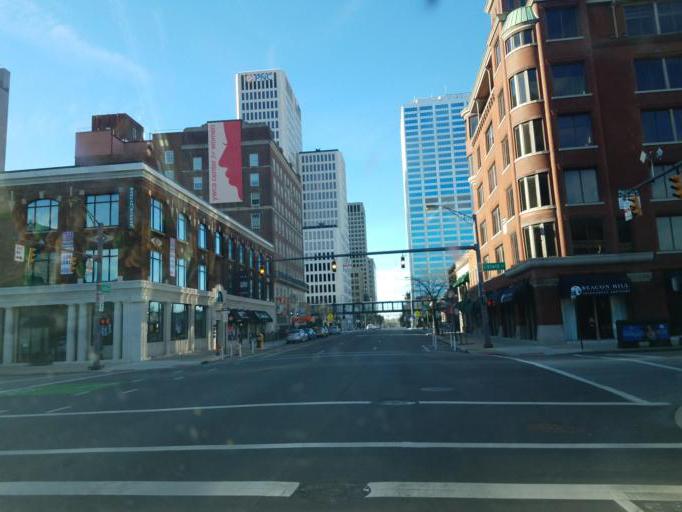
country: US
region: Ohio
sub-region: Franklin County
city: Columbus
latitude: 39.9604
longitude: -82.9958
